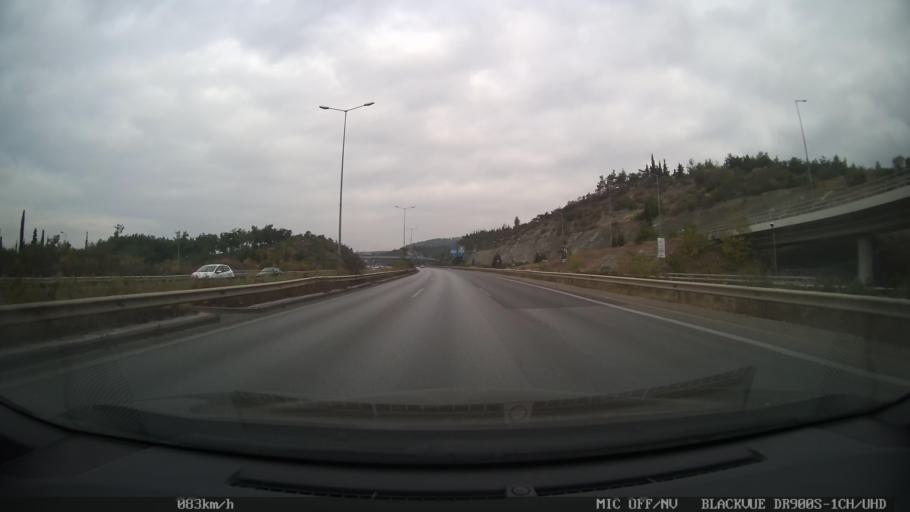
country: GR
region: Central Macedonia
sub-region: Nomos Thessalonikis
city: Triandria
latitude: 40.6227
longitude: 22.9819
